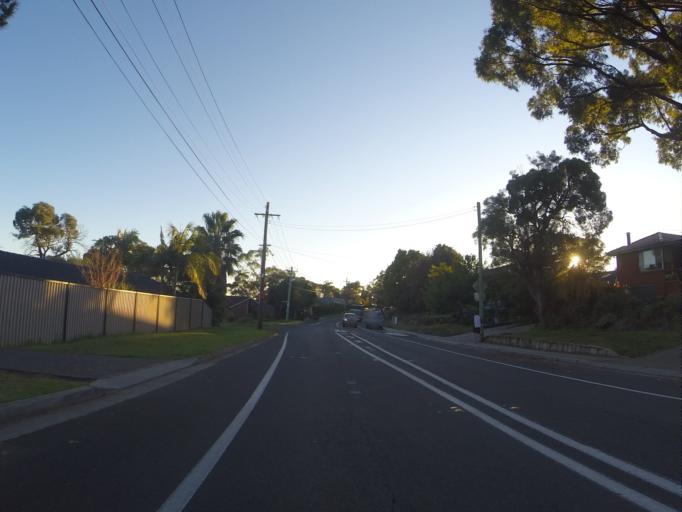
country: AU
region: New South Wales
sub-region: Sutherland Shire
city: Woronora Heights
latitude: -34.0463
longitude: 151.0161
